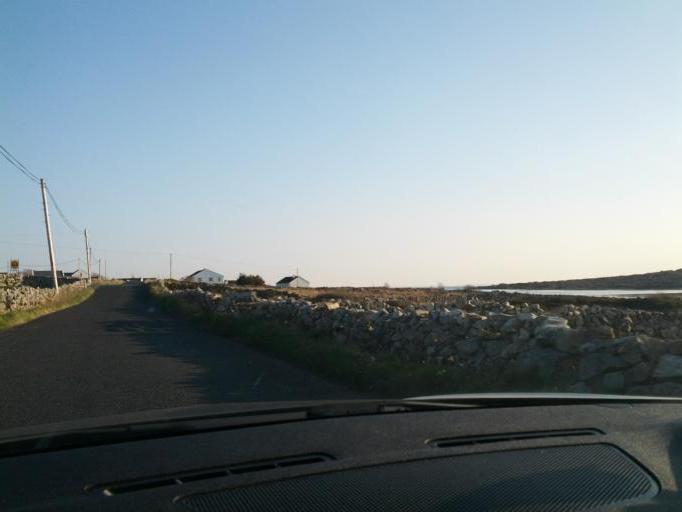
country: IE
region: Connaught
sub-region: County Galway
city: Oughterard
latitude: 53.2625
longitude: -9.5456
